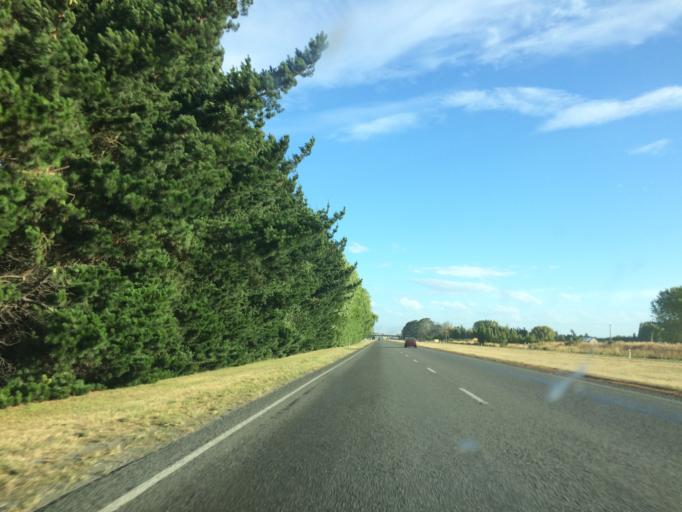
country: NZ
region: Canterbury
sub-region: Waimakariri District
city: Kaiapoi
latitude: -43.3996
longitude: 172.6424
